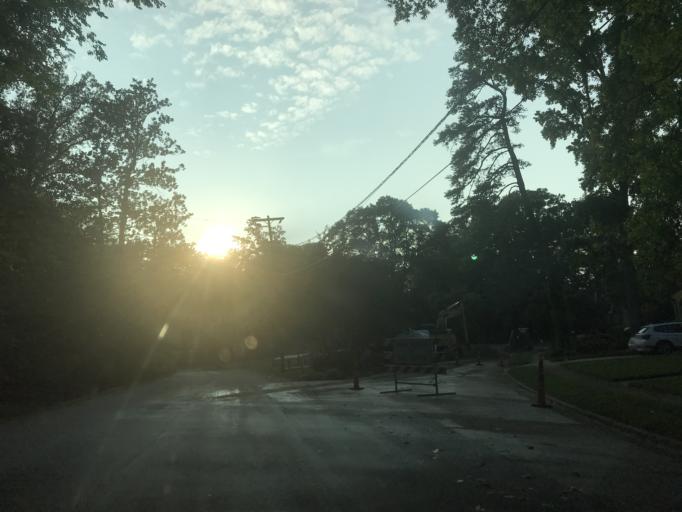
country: US
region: North Carolina
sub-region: Wake County
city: West Raleigh
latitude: 35.7985
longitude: -78.6494
